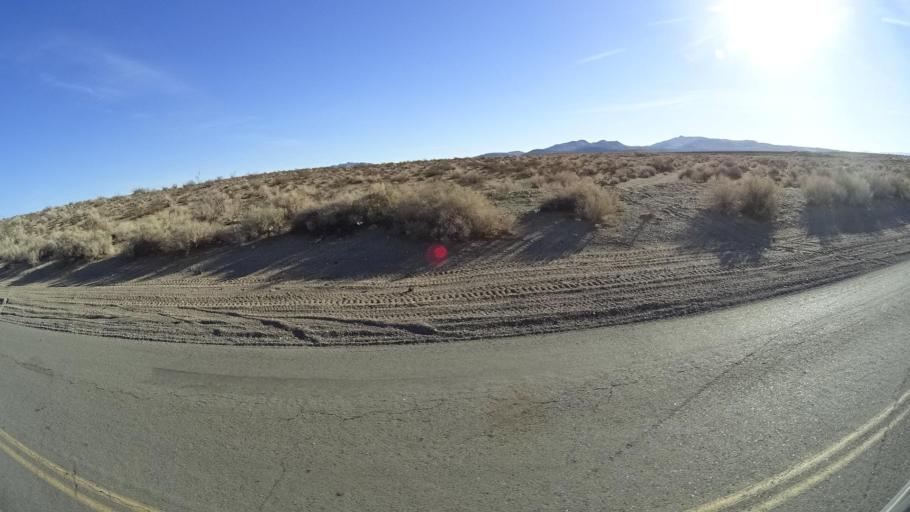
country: US
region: California
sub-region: Kern County
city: China Lake Acres
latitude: 35.6077
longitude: -117.7492
